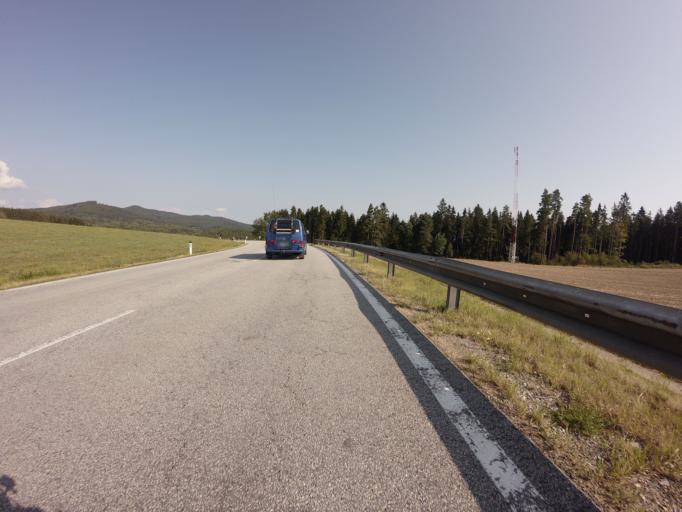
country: AT
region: Upper Austria
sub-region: Politischer Bezirk Urfahr-Umgebung
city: Bad Leonfelden
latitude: 48.5572
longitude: 14.3243
